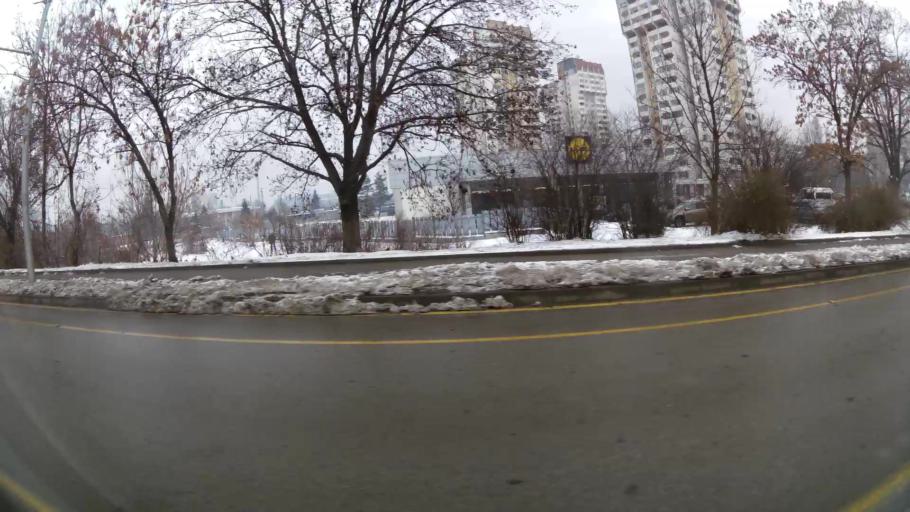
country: BG
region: Sofia-Capital
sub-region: Stolichna Obshtina
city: Sofia
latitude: 42.7113
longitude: 23.2913
